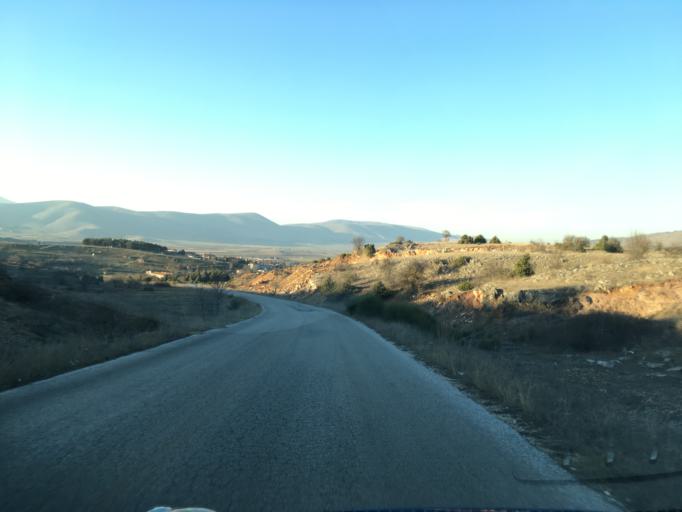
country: GR
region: West Macedonia
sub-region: Nomos Kozanis
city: Kozani
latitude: 40.2778
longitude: 21.7344
